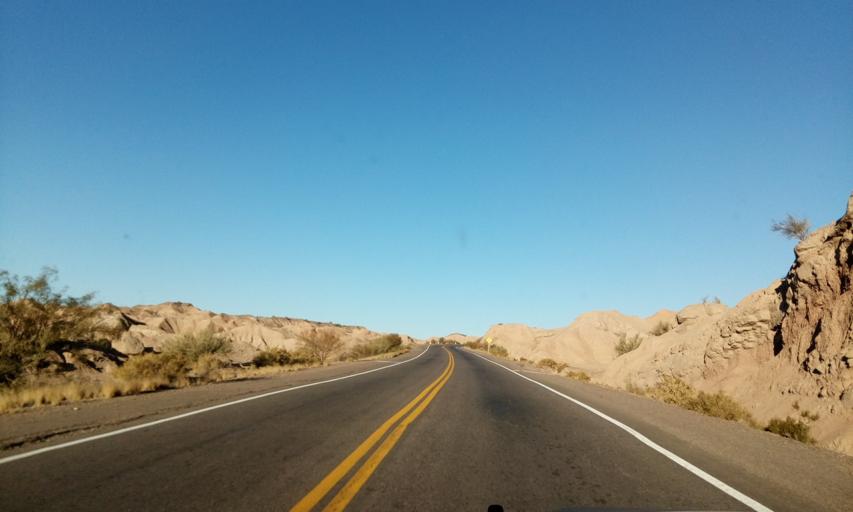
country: AR
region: San Juan
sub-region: Departamento de Rivadavia
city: Rivadavia
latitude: -31.4484
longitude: -68.6412
